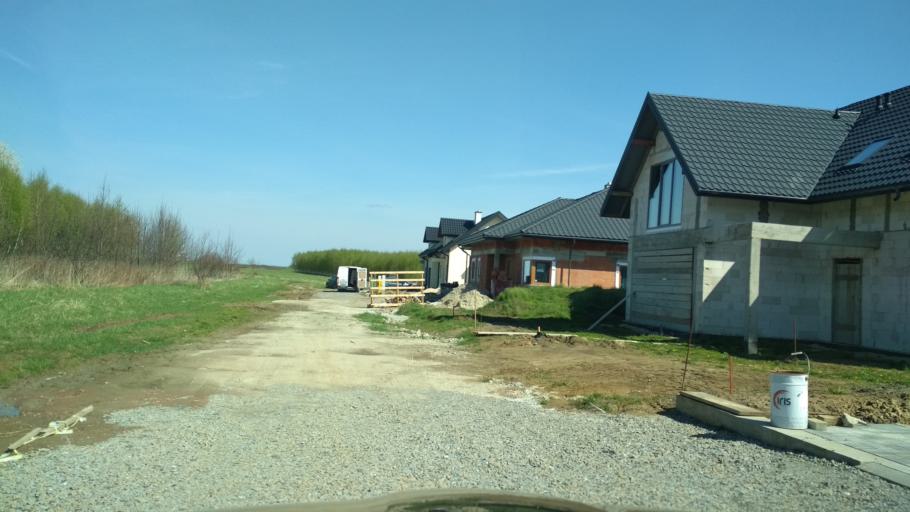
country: PL
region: Subcarpathian Voivodeship
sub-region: Powiat rzeszowski
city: Rudna Wielka
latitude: 50.0631
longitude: 21.9497
